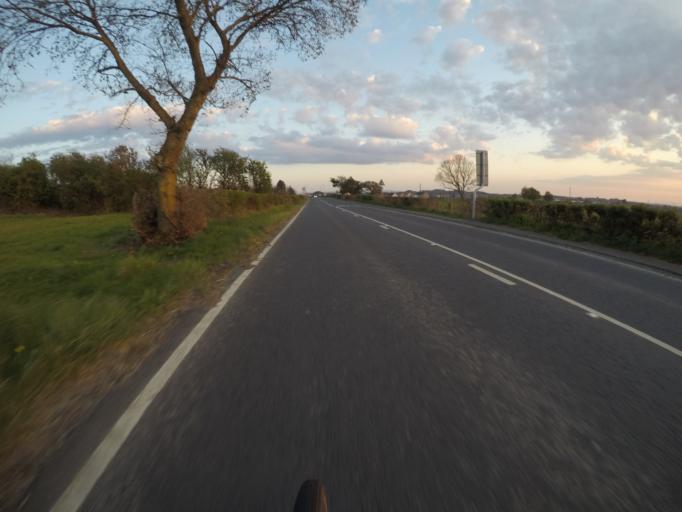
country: GB
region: Scotland
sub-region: South Ayrshire
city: Troon
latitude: 55.5552
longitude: -4.6259
